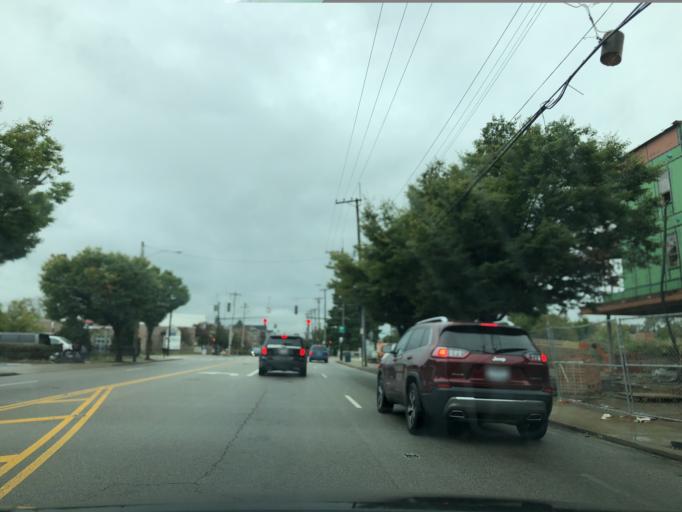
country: US
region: Ohio
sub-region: Hamilton County
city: Saint Bernard
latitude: 39.1452
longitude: -84.4904
